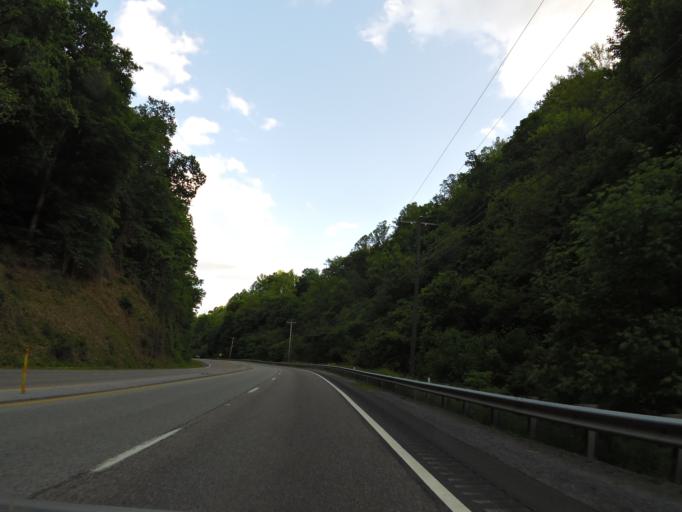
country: US
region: Virginia
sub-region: Washington County
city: Abingdon
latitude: 36.7535
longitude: -82.0571
